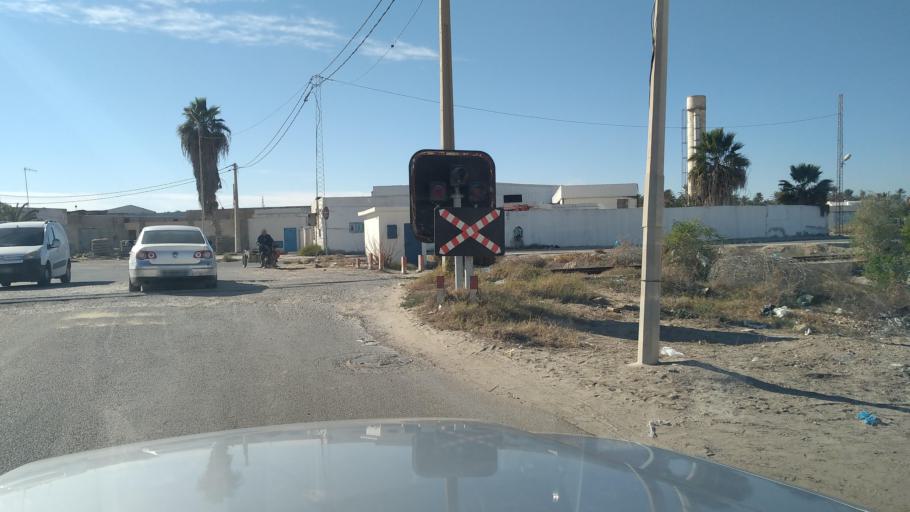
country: TN
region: Qabis
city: Gabes
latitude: 33.8930
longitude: 10.1116
